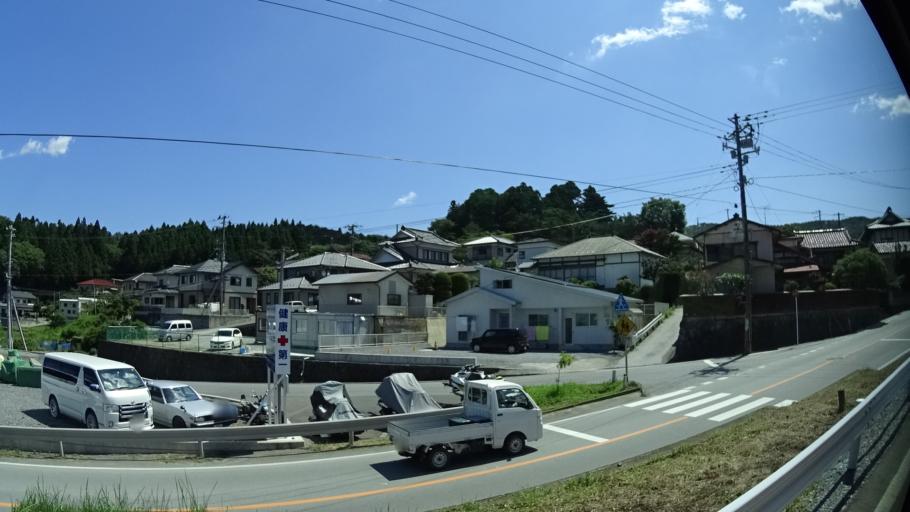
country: JP
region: Iwate
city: Ofunato
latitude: 39.0136
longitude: 141.7157
